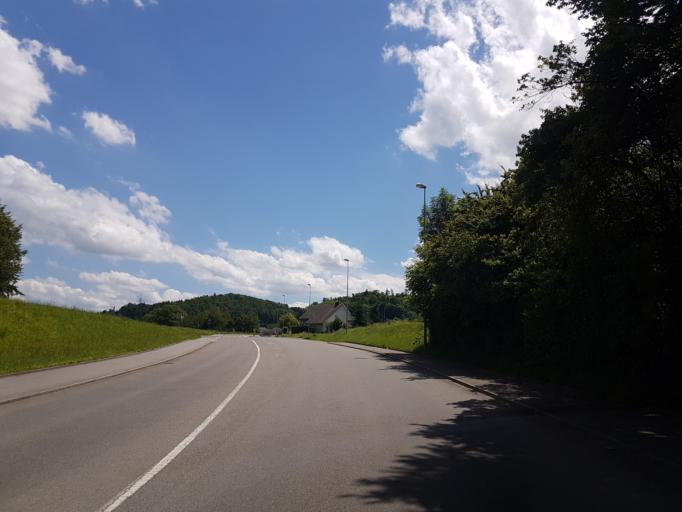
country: CH
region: Aargau
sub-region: Bezirk Lenzburg
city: Othmarsingen
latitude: 47.4136
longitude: 8.2336
